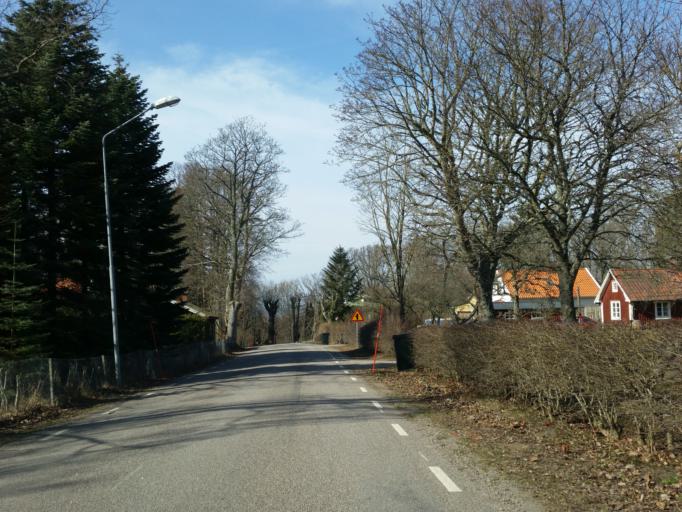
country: SE
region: Kalmar
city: Faerjestaden
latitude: 56.7543
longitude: 16.5411
